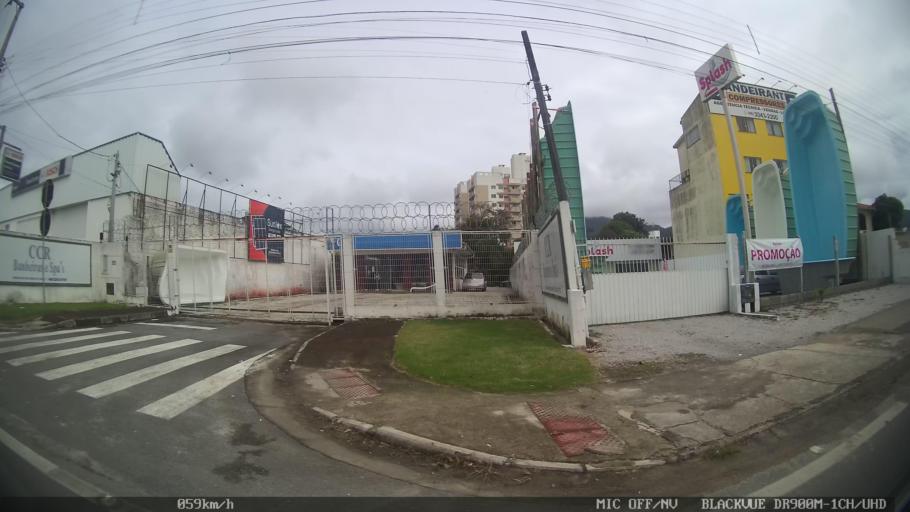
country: BR
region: Santa Catarina
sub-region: Biguacu
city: Biguacu
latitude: -27.5092
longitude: -48.6455
